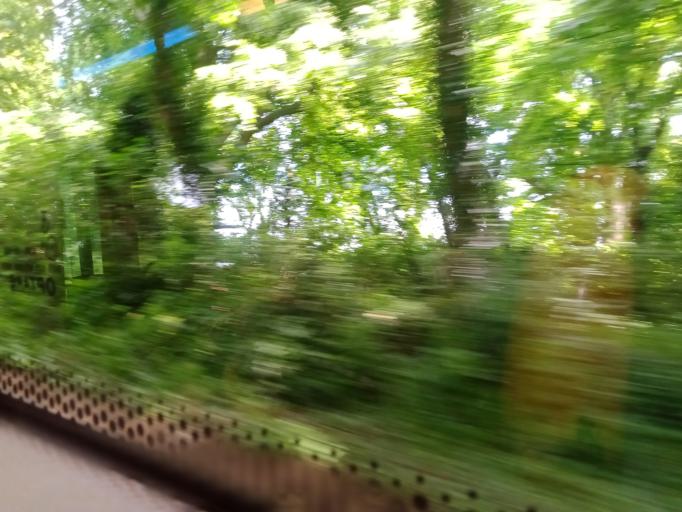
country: GB
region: Wales
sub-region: Anglesey
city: Beaumaris
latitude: 53.2699
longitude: -4.1130
